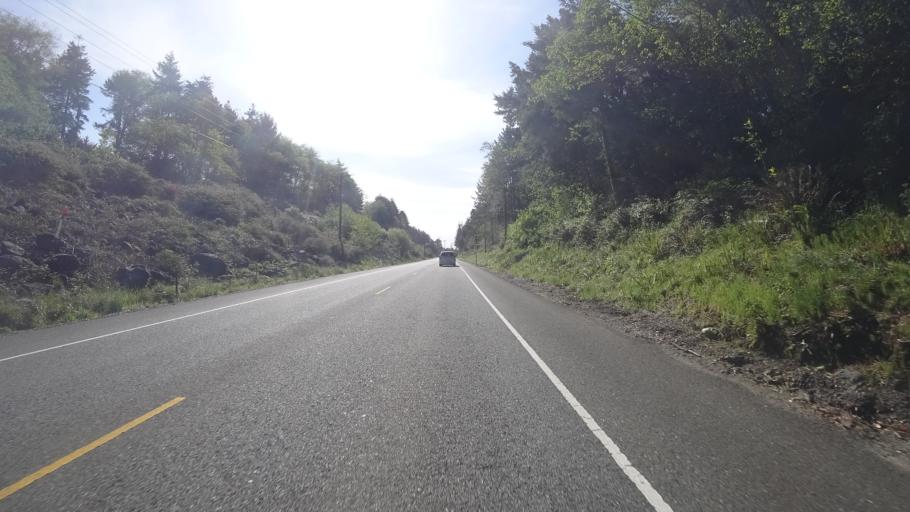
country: US
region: Oregon
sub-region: Curry County
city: Brookings
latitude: 42.0823
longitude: -124.3217
